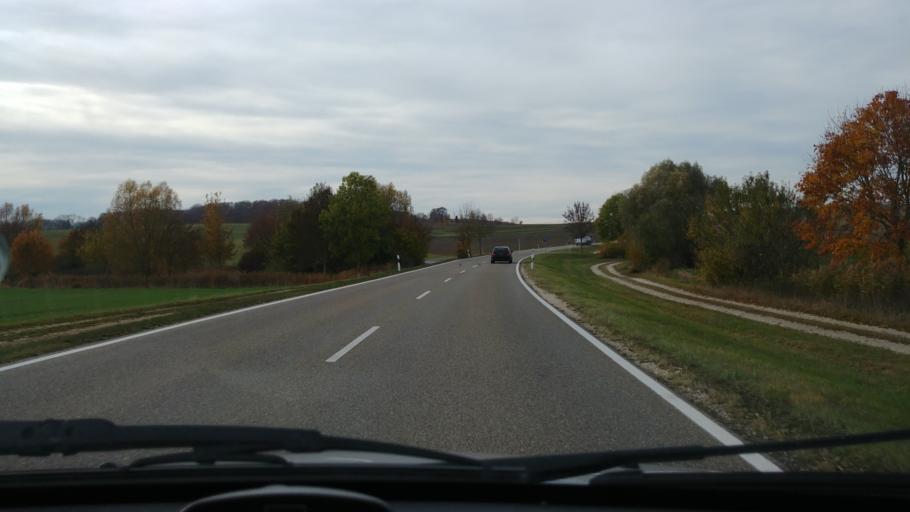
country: DE
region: Bavaria
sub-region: Swabia
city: Zoschingen
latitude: 48.6521
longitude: 10.2799
